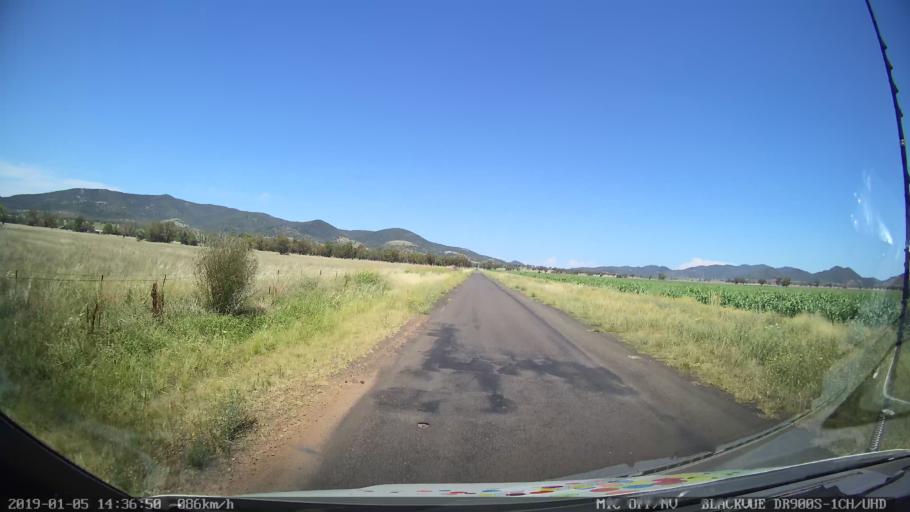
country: AU
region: New South Wales
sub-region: Tamworth Municipality
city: Phillip
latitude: -31.2455
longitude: 150.6697
